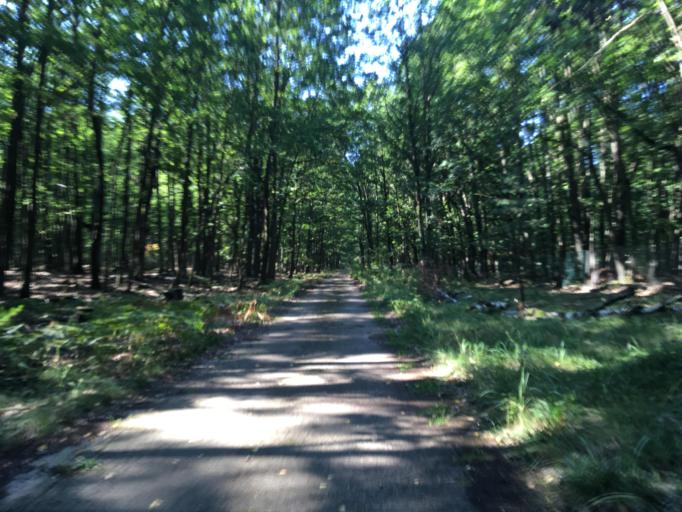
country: DE
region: Brandenburg
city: Gross Koris
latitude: 52.1964
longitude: 13.7338
